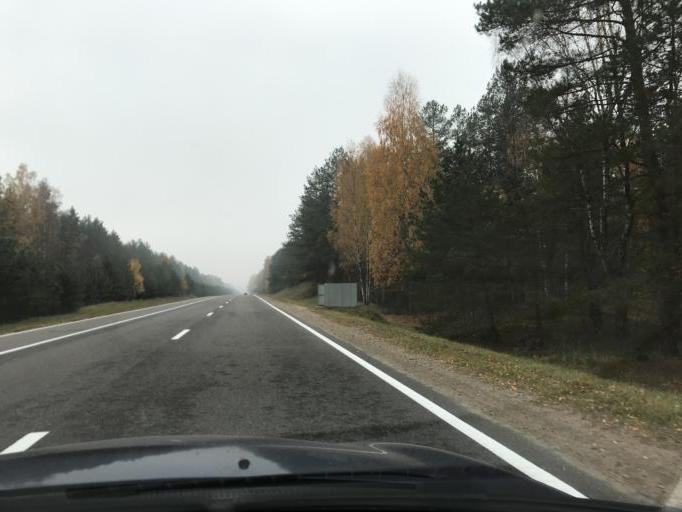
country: LT
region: Alytaus apskritis
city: Druskininkai
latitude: 53.9094
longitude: 23.9203
